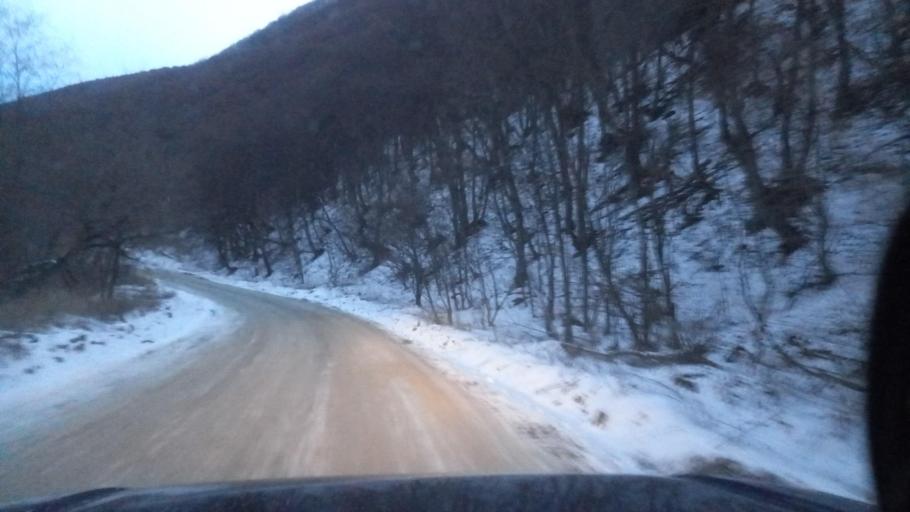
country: RU
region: Ingushetiya
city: Dzhayrakh
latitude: 42.8266
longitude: 44.6062
